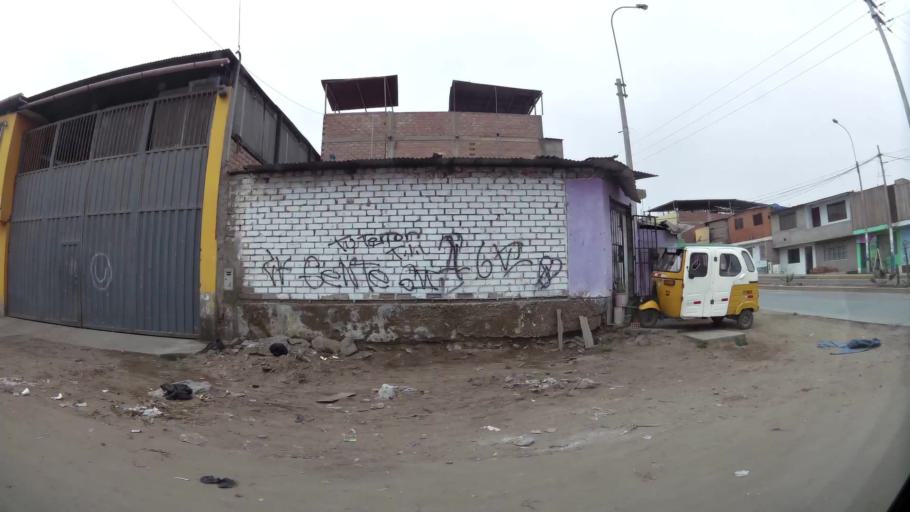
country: PE
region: Lima
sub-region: Lima
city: Surco
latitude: -12.2217
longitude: -76.9454
